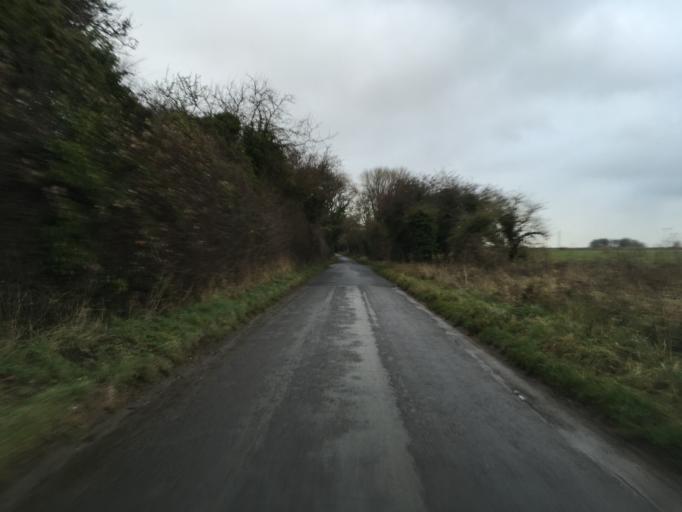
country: GB
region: England
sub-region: South Gloucestershire
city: Marshfield
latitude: 51.4991
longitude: -2.3195
